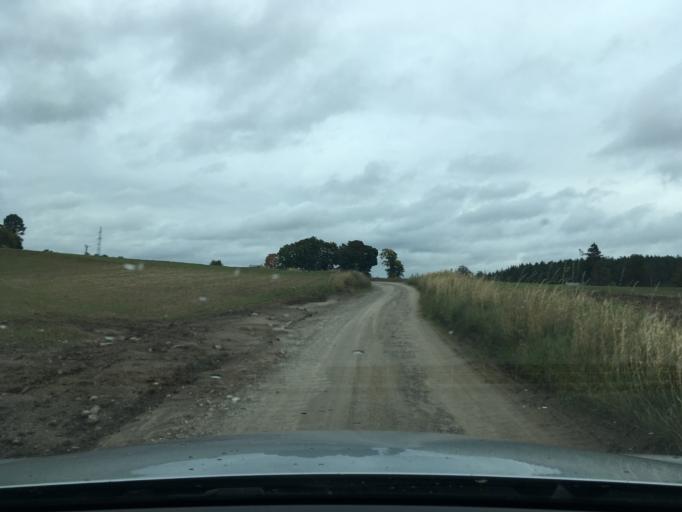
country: PL
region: Pomeranian Voivodeship
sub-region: Powiat koscierski
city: Koscierzyna
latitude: 54.1055
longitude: 17.9810
